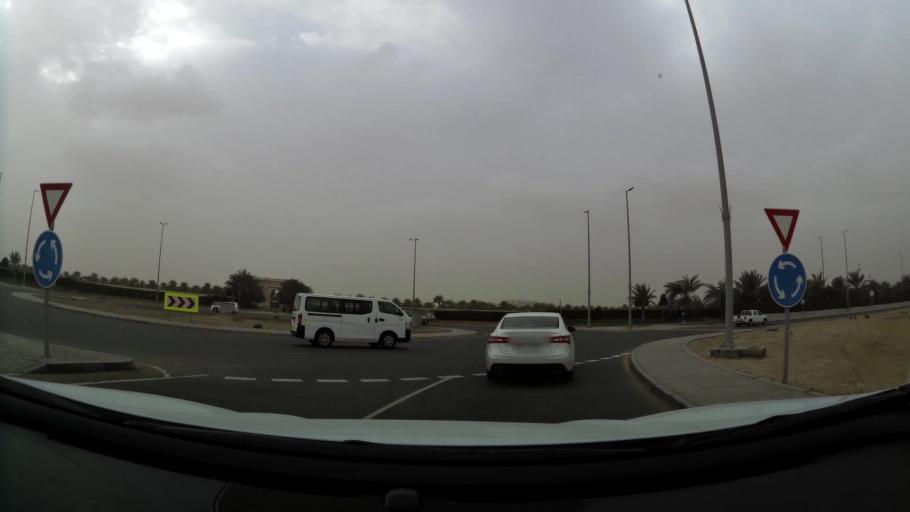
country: AE
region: Abu Dhabi
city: Abu Dhabi
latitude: 24.4251
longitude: 54.5384
